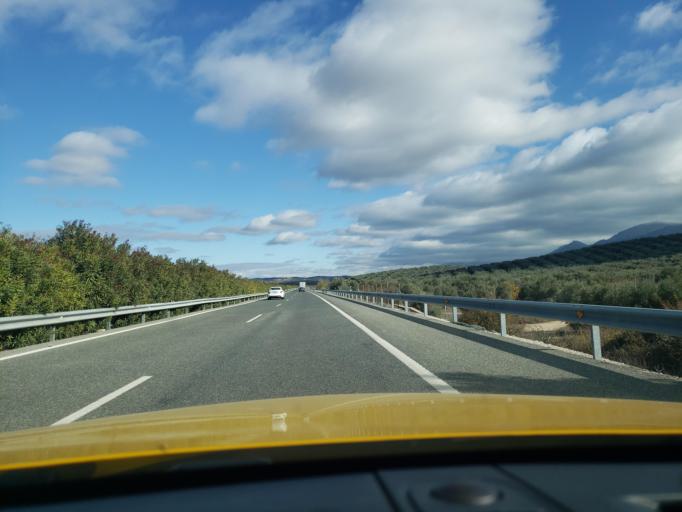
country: ES
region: Andalusia
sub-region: Provincia de Malaga
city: Villanueva del Trabuco
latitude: 37.0599
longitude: -4.3490
